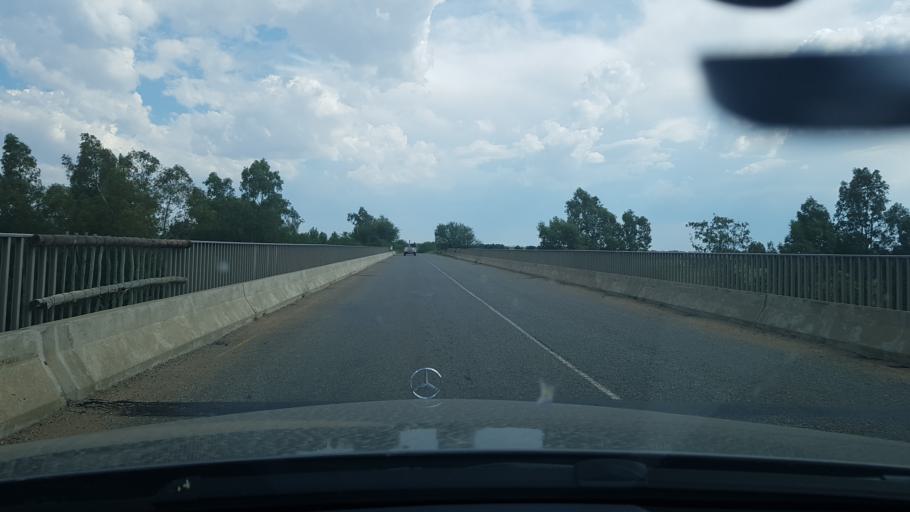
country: ZA
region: North-West
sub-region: Dr Ruth Segomotsi Mompati District Municipality
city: Bloemhof
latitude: -27.6546
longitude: 25.5953
